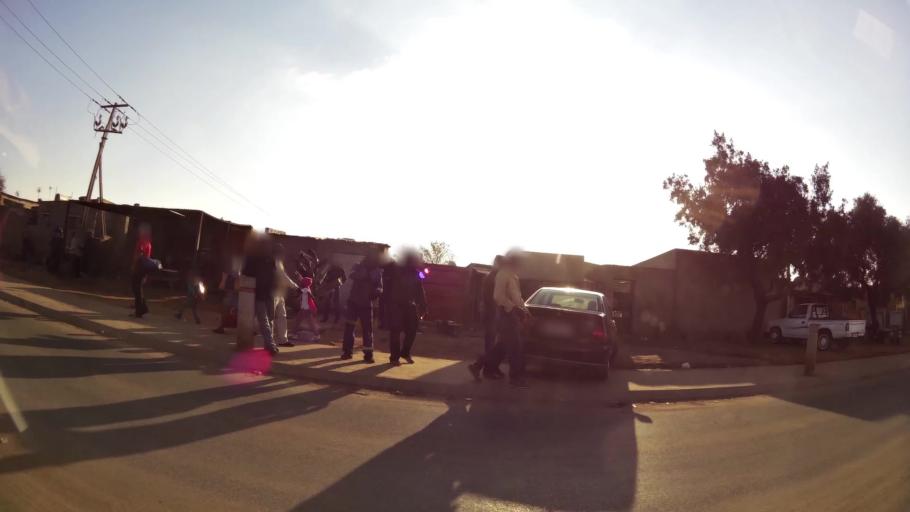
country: ZA
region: Gauteng
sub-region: Ekurhuleni Metropolitan Municipality
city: Tembisa
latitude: -25.9856
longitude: 28.2028
